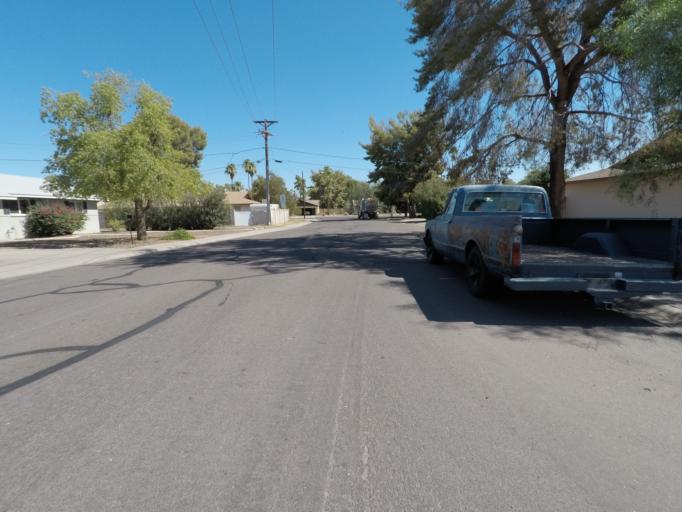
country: US
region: Arizona
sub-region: Maricopa County
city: Tempe Junction
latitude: 33.3994
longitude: -111.9426
